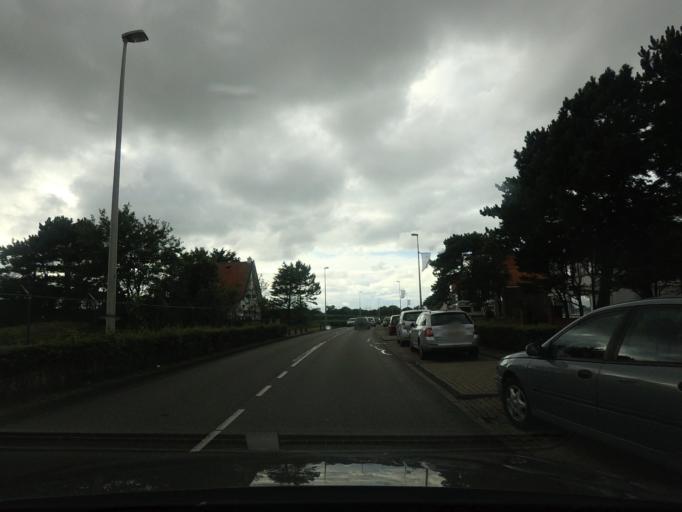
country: NL
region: North Holland
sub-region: Gemeente Zandvoort
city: Zandvoort
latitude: 52.3653
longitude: 4.5509
